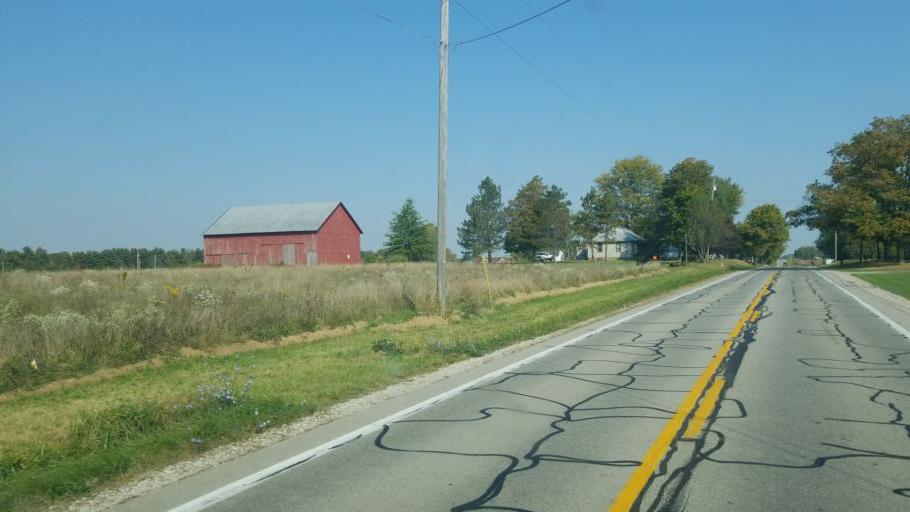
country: US
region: Ohio
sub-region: Morrow County
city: Mount Gilead
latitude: 40.5868
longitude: -82.8240
